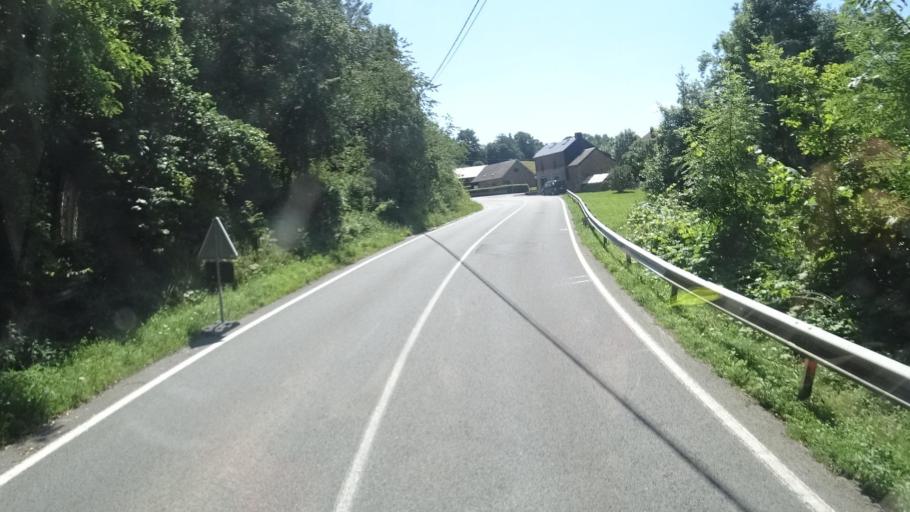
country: BE
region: Wallonia
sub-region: Province de Namur
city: Floreffe
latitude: 50.4214
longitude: 4.7622
